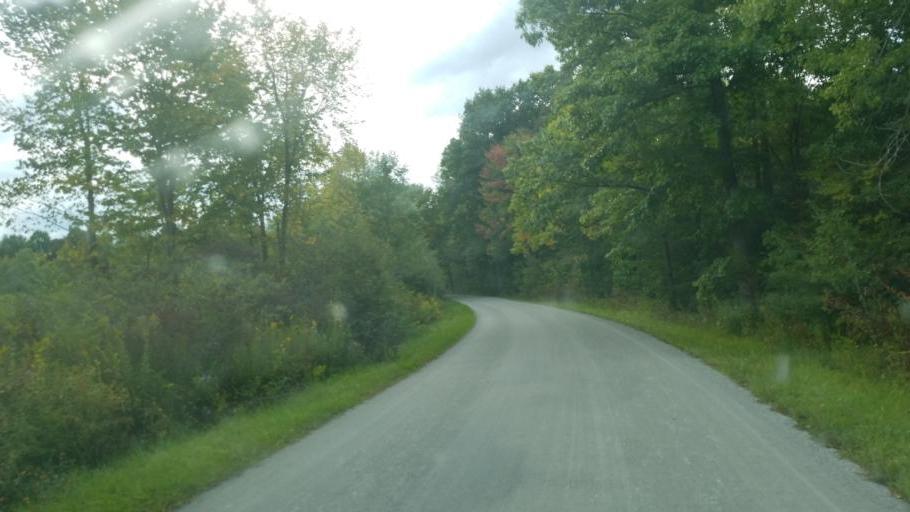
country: US
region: Pennsylvania
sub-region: Mercer County
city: Greenville
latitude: 41.4775
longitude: -80.3524
